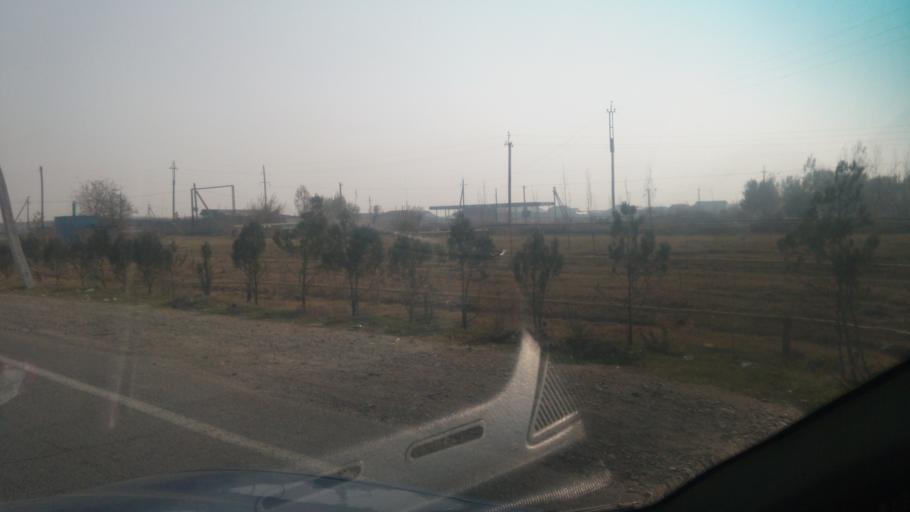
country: UZ
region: Sirdaryo
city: Guliston
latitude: 40.4883
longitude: 68.7513
